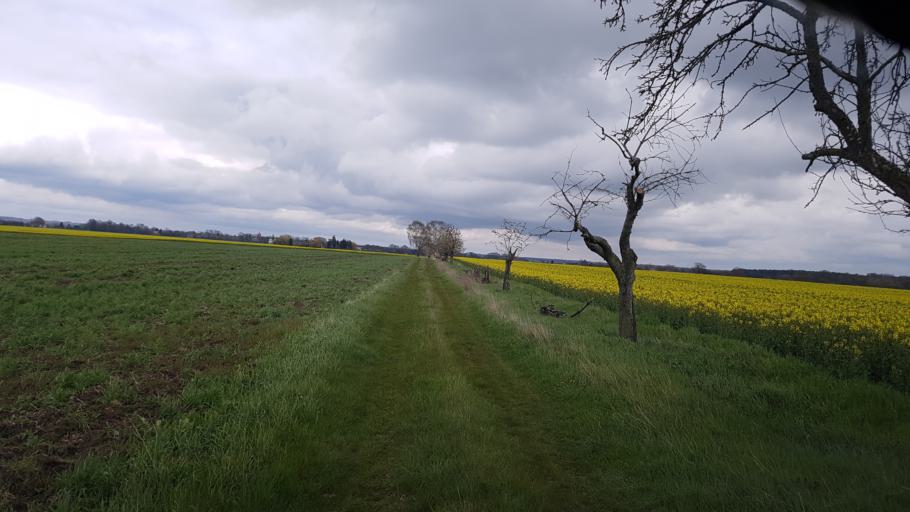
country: DE
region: Brandenburg
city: Schonborn
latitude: 51.6734
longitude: 13.4852
